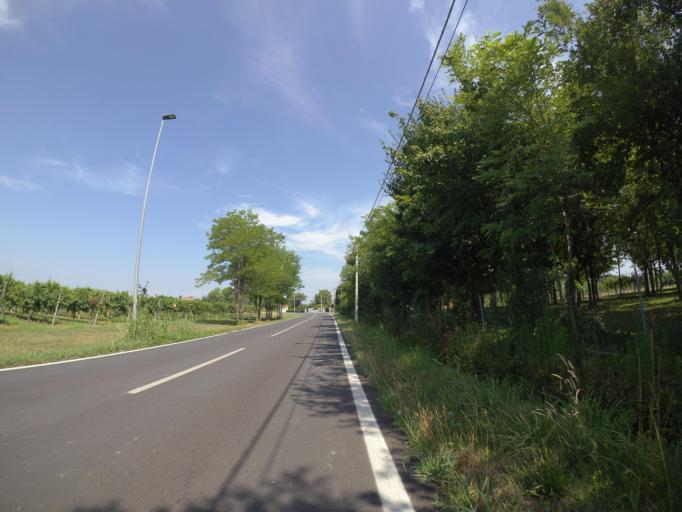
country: IT
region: Friuli Venezia Giulia
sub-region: Provincia di Pordenone
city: Ramuscello
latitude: 45.9082
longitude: 12.8912
